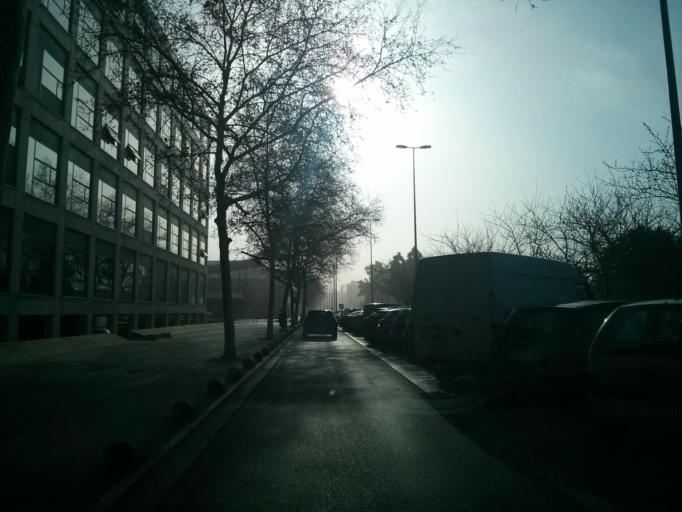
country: ES
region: Valencia
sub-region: Provincia de Valencia
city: Alboraya
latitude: 39.4803
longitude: -0.3383
